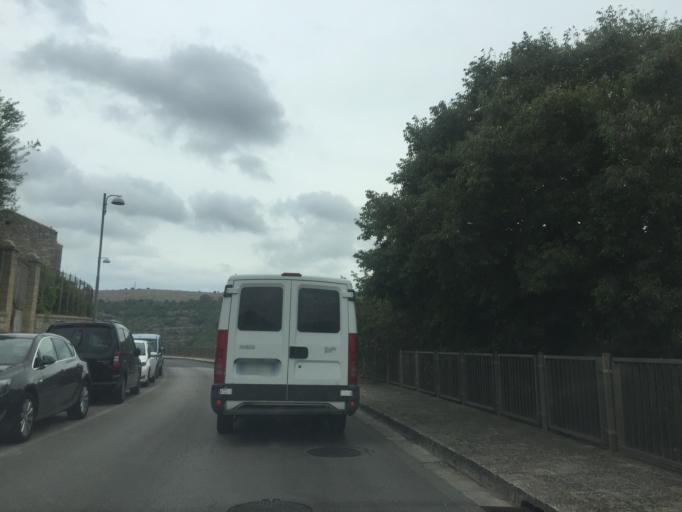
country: IT
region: Sicily
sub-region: Ragusa
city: Ragusa
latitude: 36.9243
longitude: 14.7458
